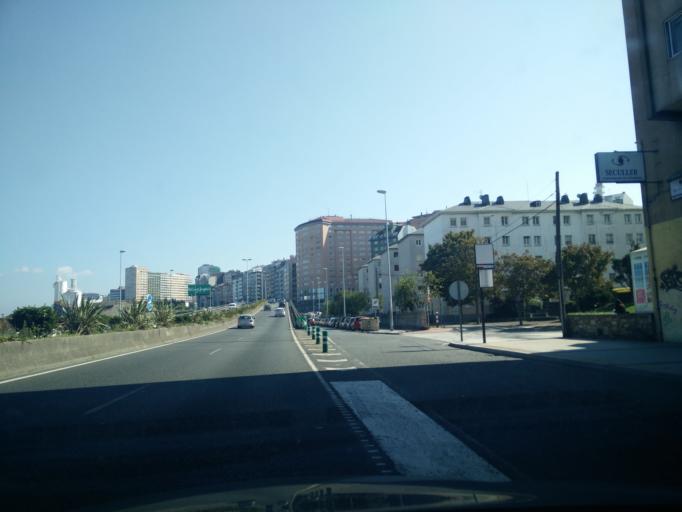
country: ES
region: Galicia
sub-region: Provincia da Coruna
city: A Coruna
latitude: 43.3565
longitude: -8.3981
